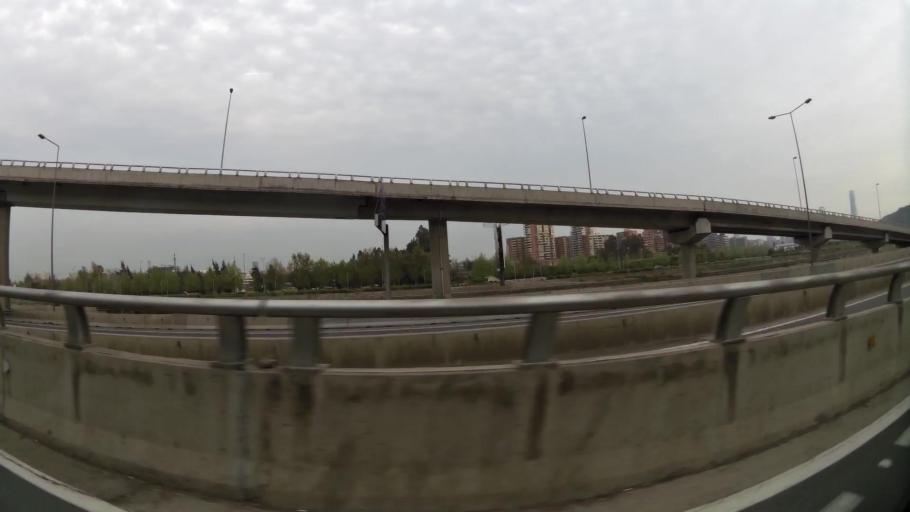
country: CL
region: Santiago Metropolitan
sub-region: Provincia de Santiago
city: Villa Presidente Frei, Nunoa, Santiago, Chile
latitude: -33.3914
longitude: -70.6015
